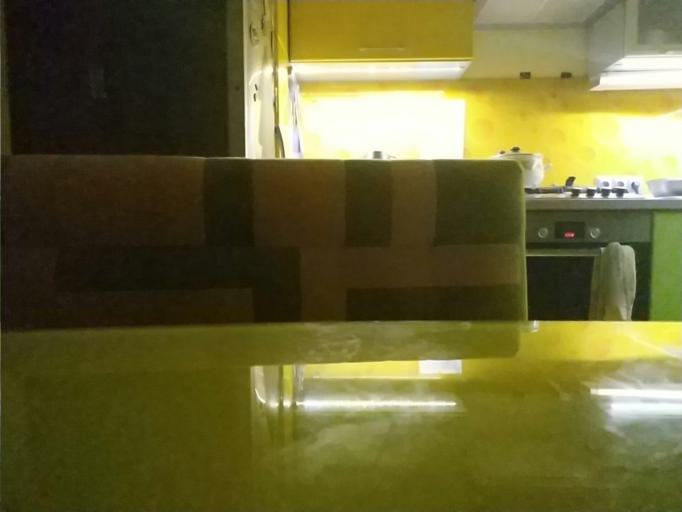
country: RU
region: Republic of Karelia
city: Pyaozerskiy
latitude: 65.6337
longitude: 30.5490
